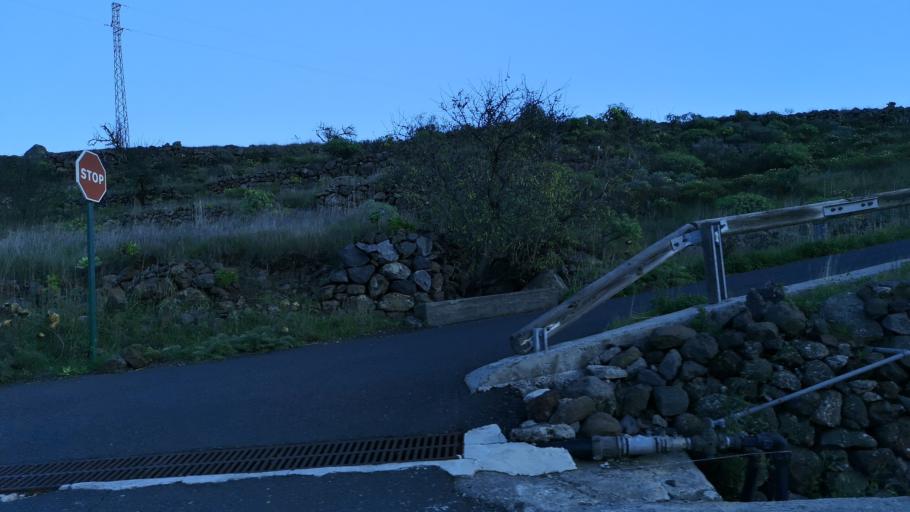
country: ES
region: Canary Islands
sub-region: Provincia de Santa Cruz de Tenerife
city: Alajero
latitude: 28.0709
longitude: -17.2378
